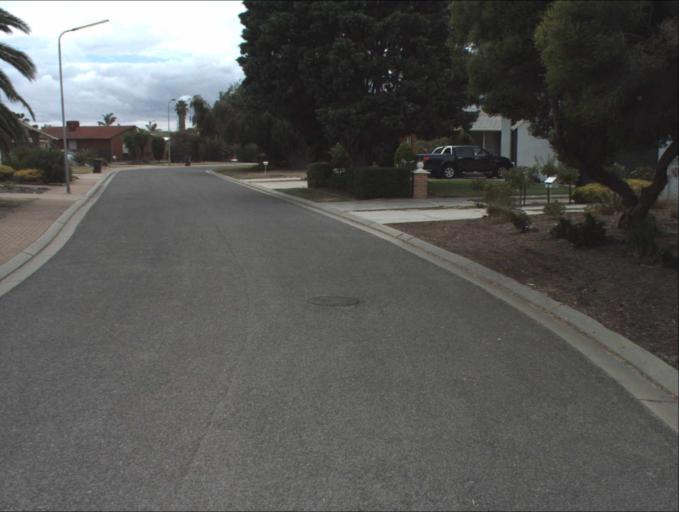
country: AU
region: South Australia
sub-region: Port Adelaide Enfield
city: Birkenhead
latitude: -34.7881
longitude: 138.4990
